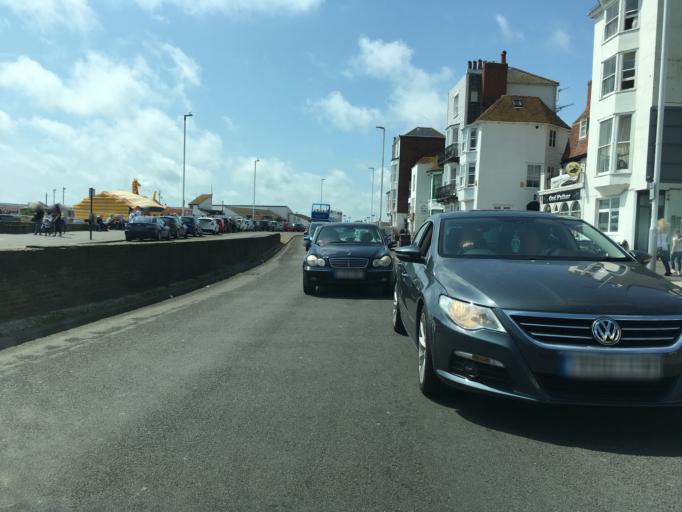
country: GB
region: England
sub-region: East Sussex
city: Hastings
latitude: 50.8559
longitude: 0.5899
